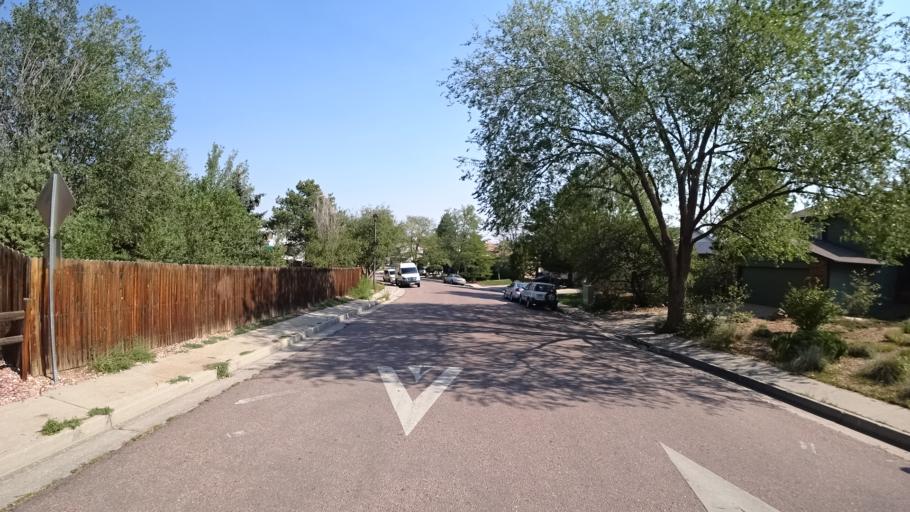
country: US
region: Colorado
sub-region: El Paso County
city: Stratmoor
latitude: 38.7837
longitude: -104.8140
